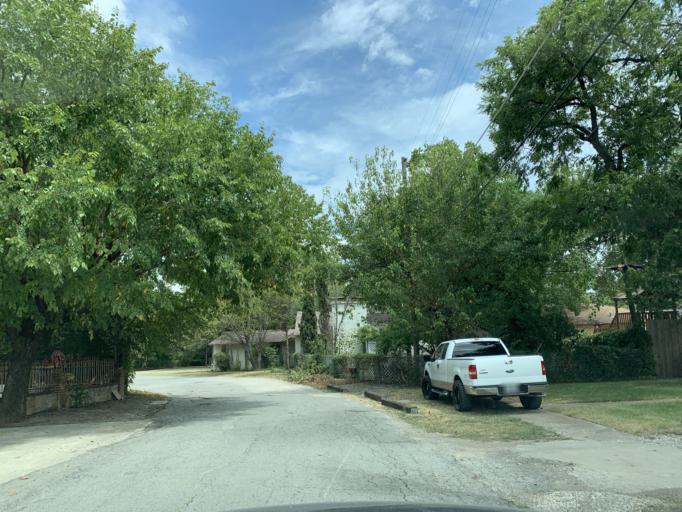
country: US
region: Texas
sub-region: Dallas County
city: Cockrell Hill
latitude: 32.7392
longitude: -96.8788
